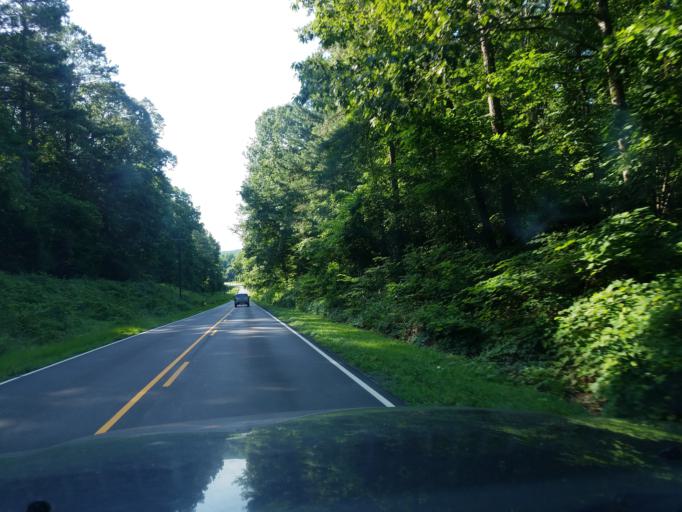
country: US
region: North Carolina
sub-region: Granville County
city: Butner
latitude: 36.1605
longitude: -78.7776
